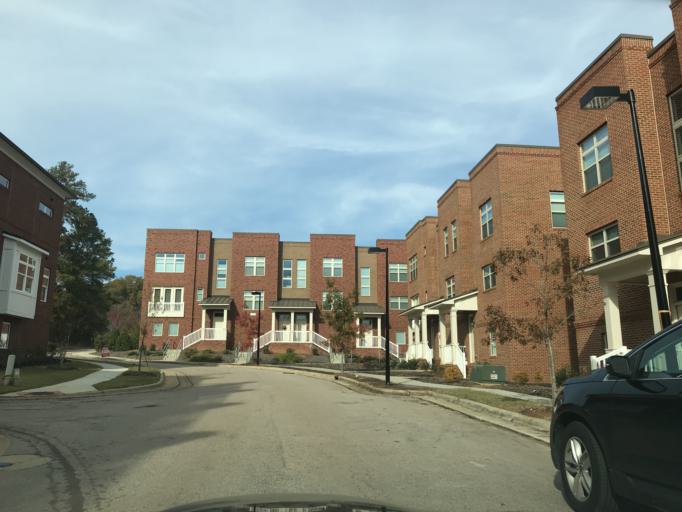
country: US
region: North Carolina
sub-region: Wake County
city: West Raleigh
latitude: 35.7685
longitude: -78.6813
